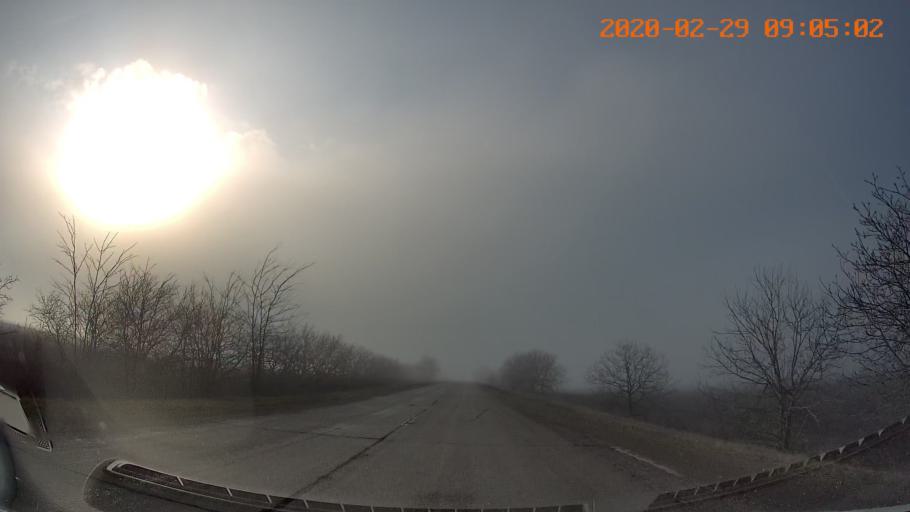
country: MD
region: Telenesti
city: Tiraspolul Nou
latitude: 46.8945
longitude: 29.7386
